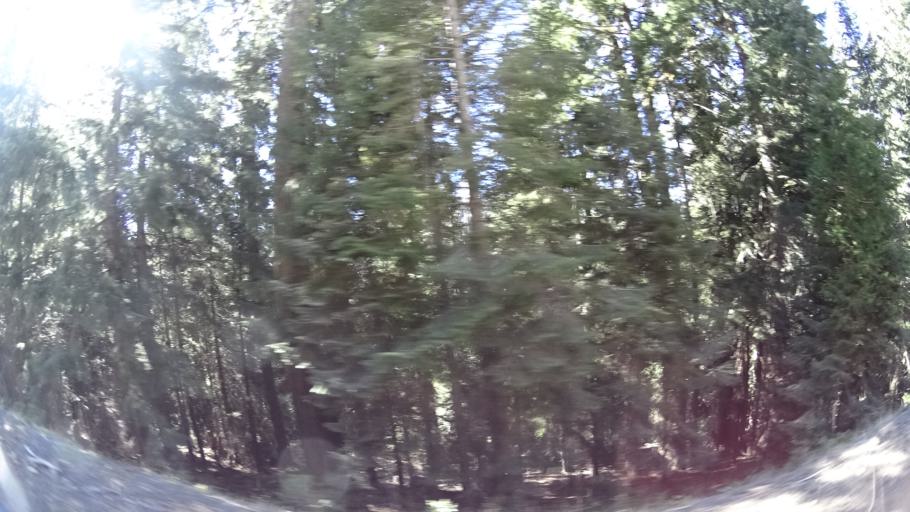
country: US
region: California
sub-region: Trinity County
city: Weaverville
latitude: 41.2270
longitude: -122.9282
